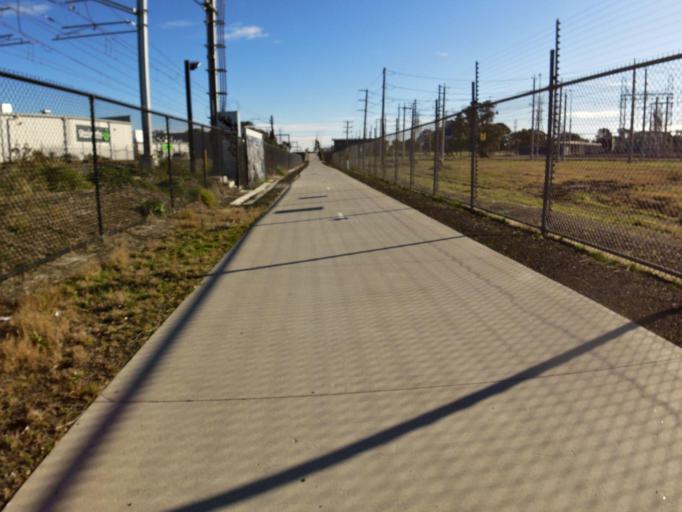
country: AU
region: Victoria
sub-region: Whittlesea
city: Mill Park
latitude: -37.6480
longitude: 145.0756
